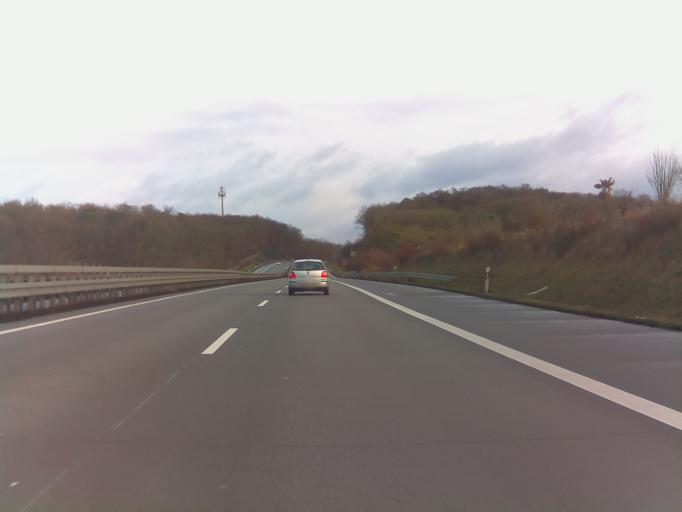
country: DE
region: Hesse
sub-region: Regierungsbezirk Darmstadt
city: Munzenberg
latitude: 50.5053
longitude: 8.7434
